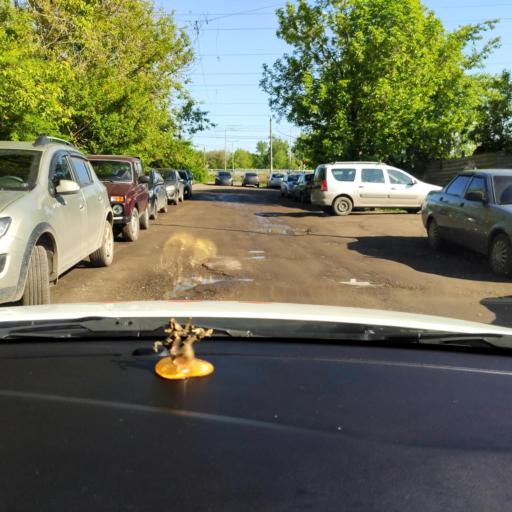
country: RU
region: Tatarstan
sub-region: Gorod Kazan'
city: Kazan
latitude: 55.8445
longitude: 49.0988
